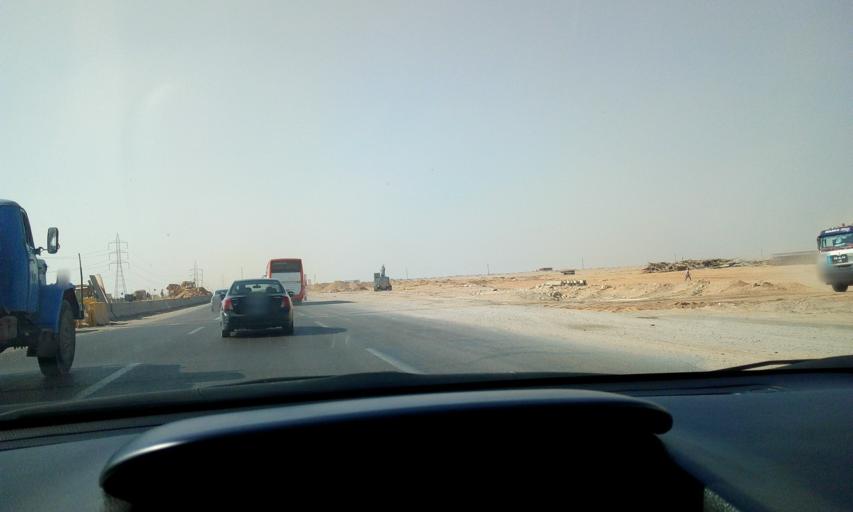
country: EG
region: Al Jizah
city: Madinat Sittah Uktubar
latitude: 29.8681
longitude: 31.0721
